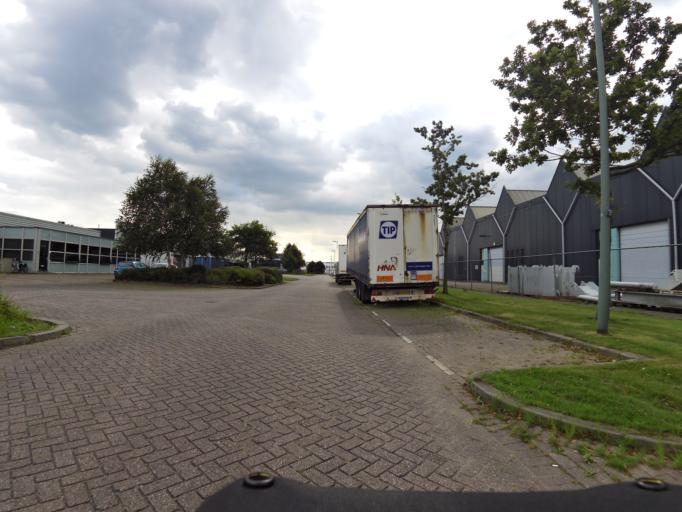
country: NL
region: South Holland
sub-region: Gemeente Vlaardingen
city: Vlaardingen
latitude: 51.8997
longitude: 4.3173
